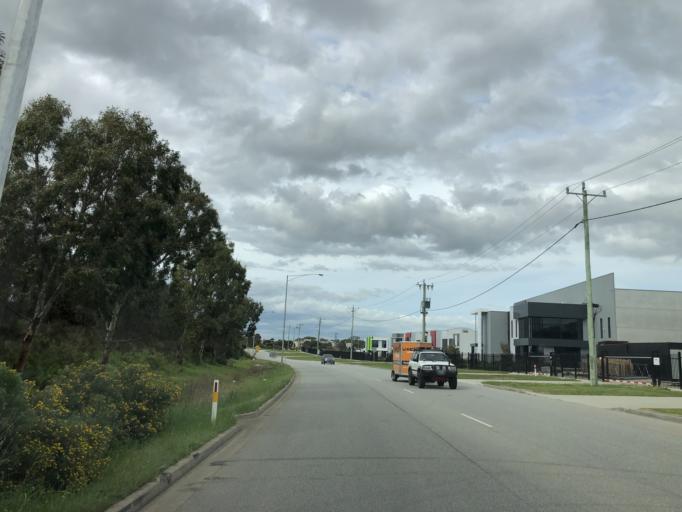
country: AU
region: Victoria
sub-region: Frankston
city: Carrum Downs
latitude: -38.0862
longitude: 145.1716
